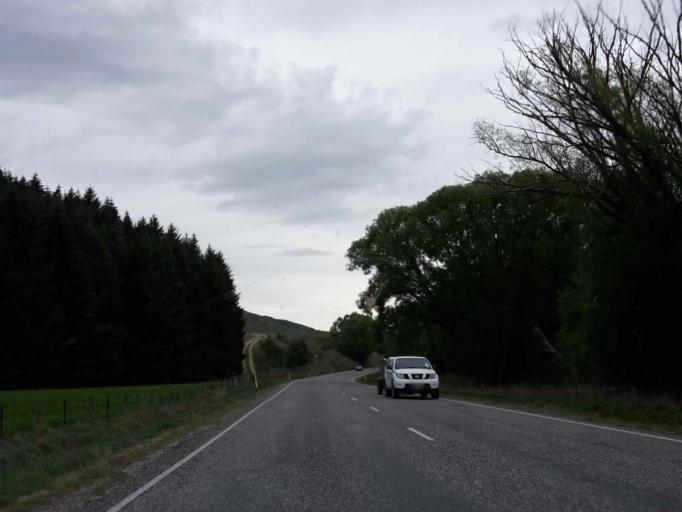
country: NZ
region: Otago
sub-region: Queenstown-Lakes District
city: Wanaka
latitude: -44.7646
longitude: 169.5084
